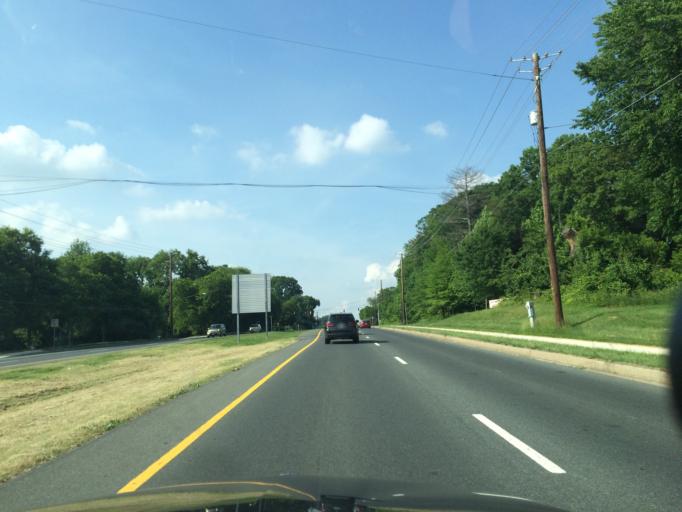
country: US
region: Maryland
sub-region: Montgomery County
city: Olney
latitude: 39.1321
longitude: -77.0704
